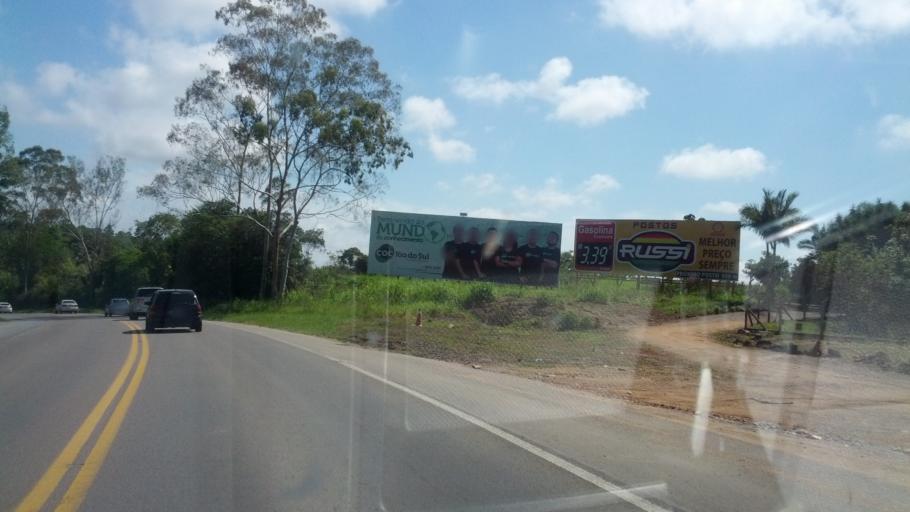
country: BR
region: Santa Catarina
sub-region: Ibirama
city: Ibirama
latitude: -27.1459
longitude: -49.5495
